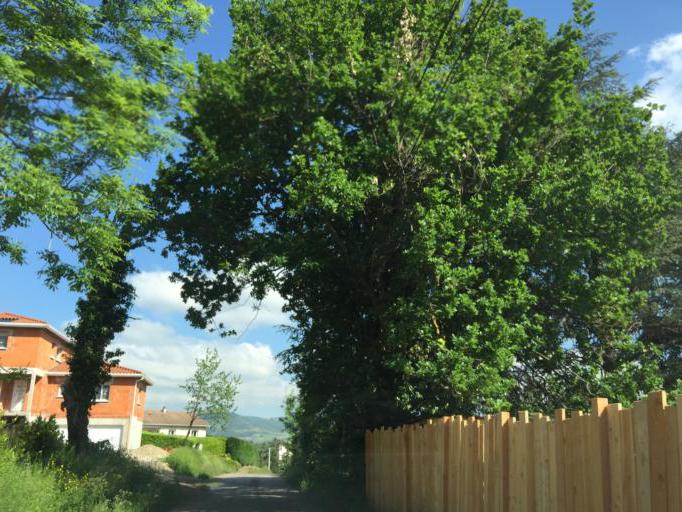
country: FR
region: Rhone-Alpes
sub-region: Departement de la Loire
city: Saint-Chamond
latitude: 45.4653
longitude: 4.5355
